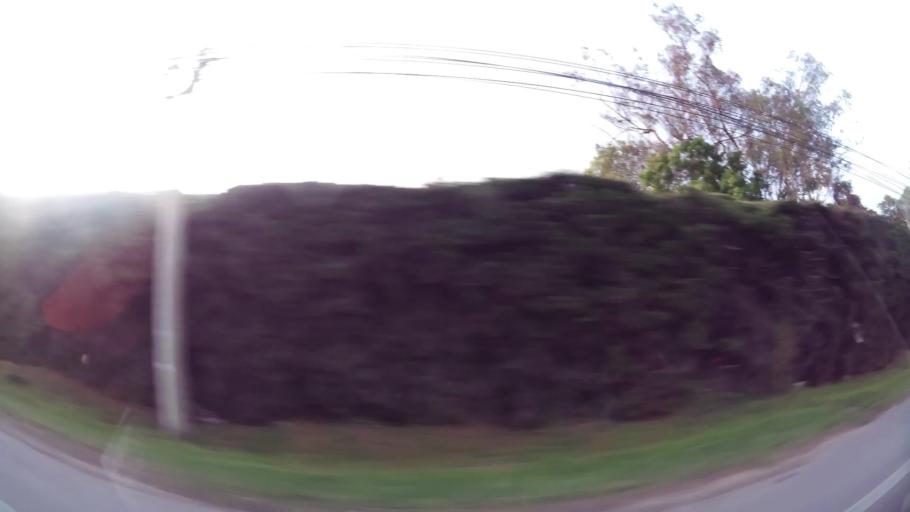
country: CO
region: Cundinamarca
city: Cota
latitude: 4.7882
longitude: -74.1207
